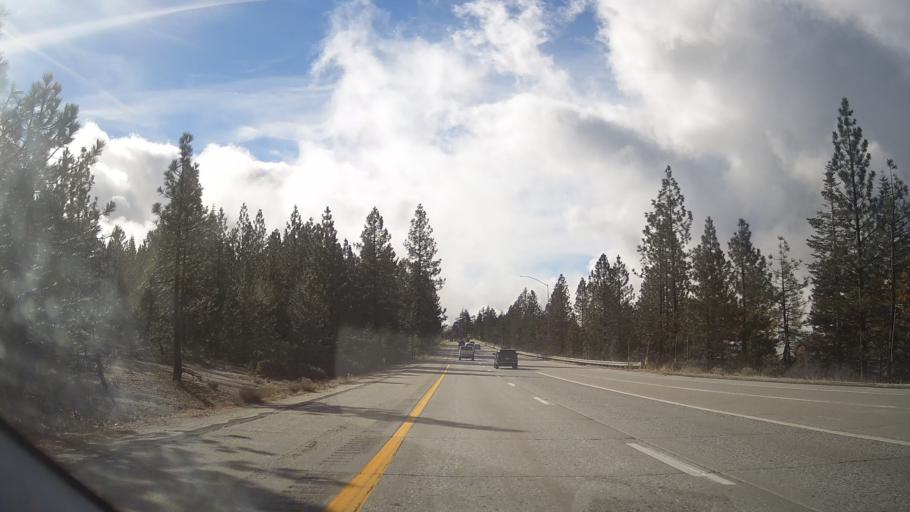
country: US
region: California
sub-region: Placer County
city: Foresthill
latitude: 39.2834
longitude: -120.7060
